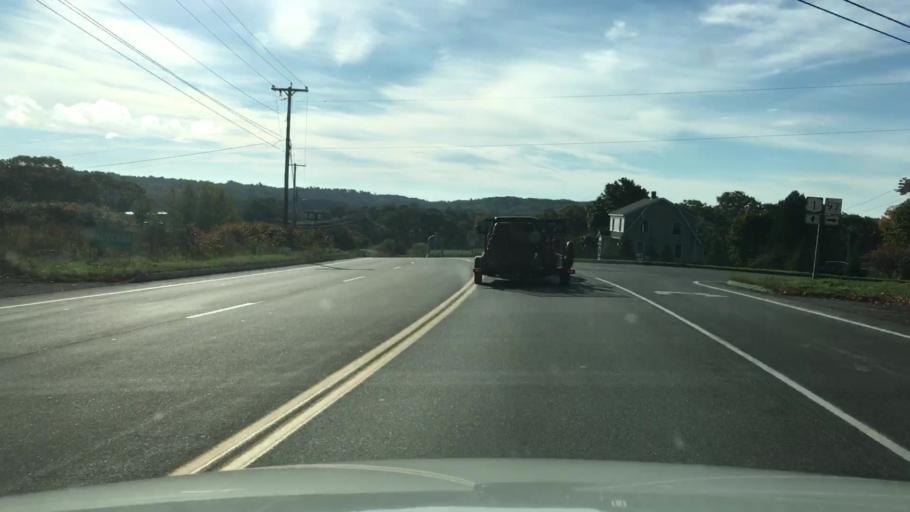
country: US
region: Maine
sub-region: Knox County
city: Warren
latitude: 44.0809
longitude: -69.2253
